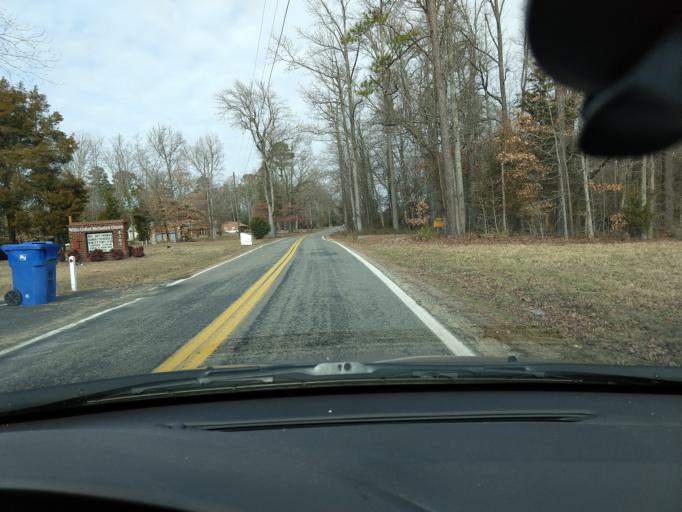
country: US
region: Virginia
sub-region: Henrico County
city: Fort Lee
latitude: 37.4345
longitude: -77.2356
